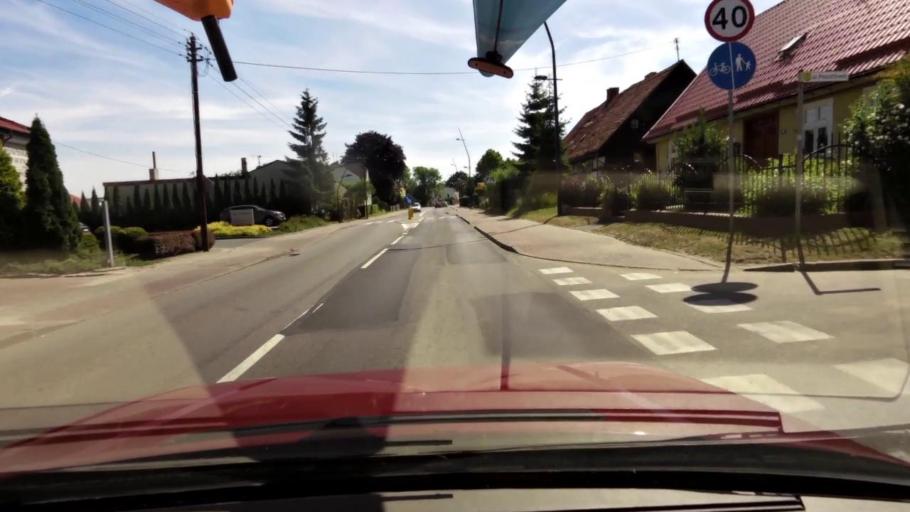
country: PL
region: Pomeranian Voivodeship
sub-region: Powiat slupski
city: Kobylnica
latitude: 54.4420
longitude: 16.9994
